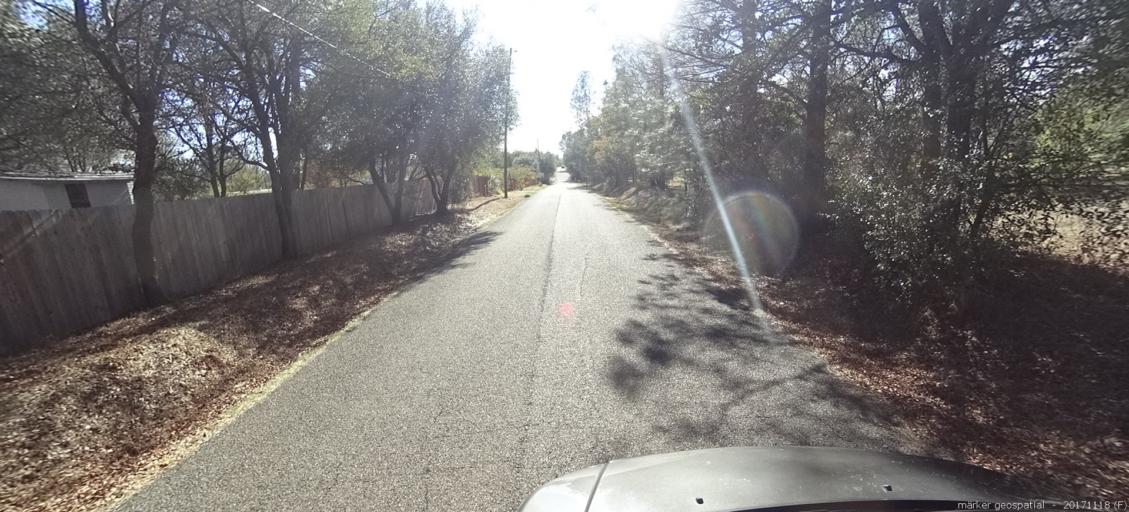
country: US
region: California
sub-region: Shasta County
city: Anderson
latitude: 40.4349
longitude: -122.3976
